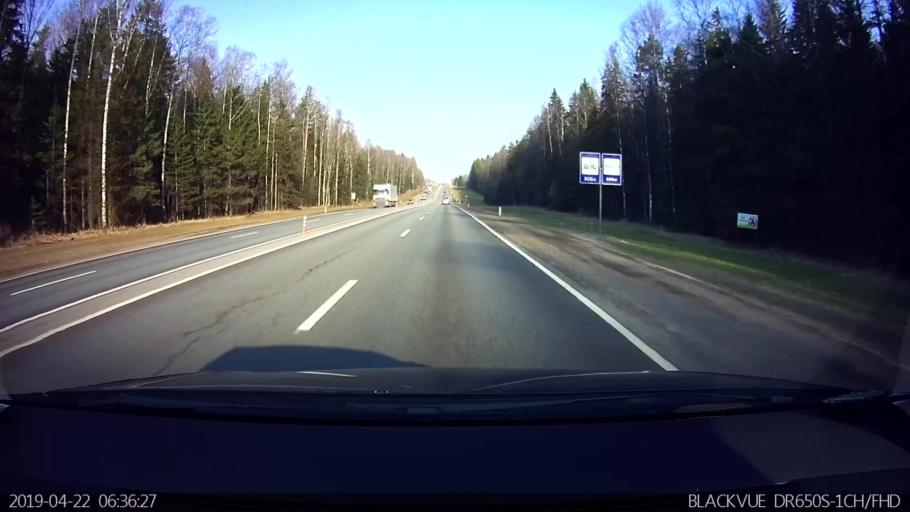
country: RU
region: Moskovskaya
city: Uvarovka
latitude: 55.4847
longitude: 35.4284
